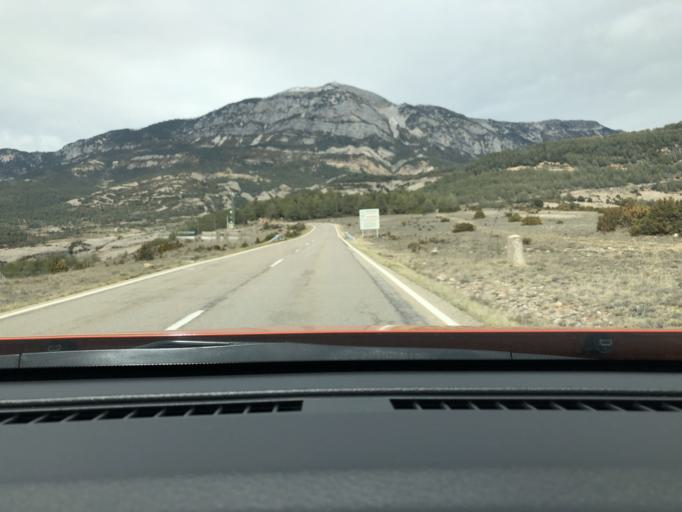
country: ES
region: Catalonia
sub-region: Provincia de Lleida
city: Olius
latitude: 42.1233
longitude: 1.5442
